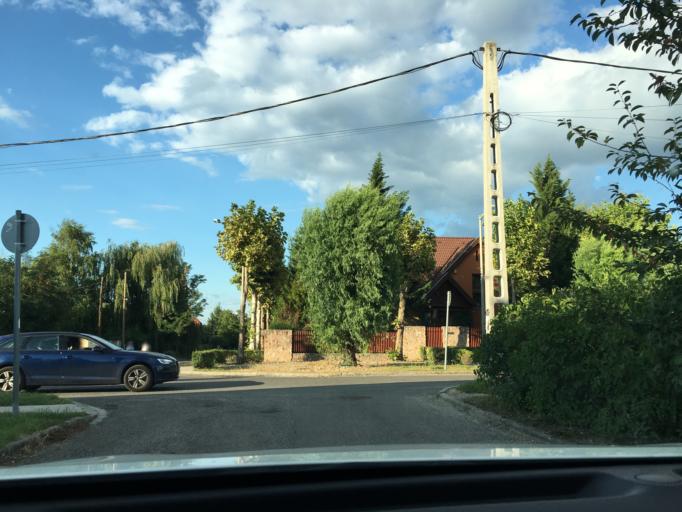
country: HU
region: Budapest
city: Budapest XVII. keruelet
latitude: 47.4742
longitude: 19.2626
